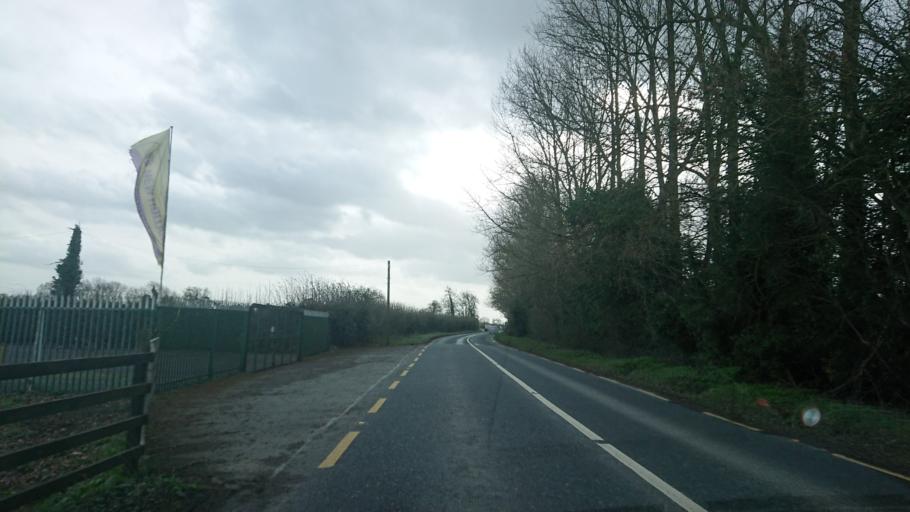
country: IE
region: Leinster
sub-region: Kildare
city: Naas
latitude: 53.1683
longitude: -6.6879
